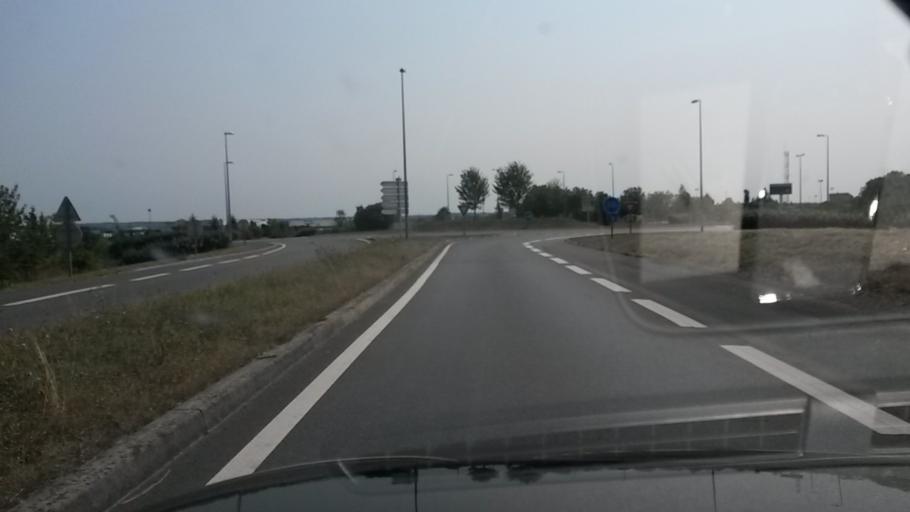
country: FR
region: Pays de la Loire
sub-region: Departement de la Loire-Atlantique
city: Saint-Gereon
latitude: 47.4037
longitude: -1.1908
